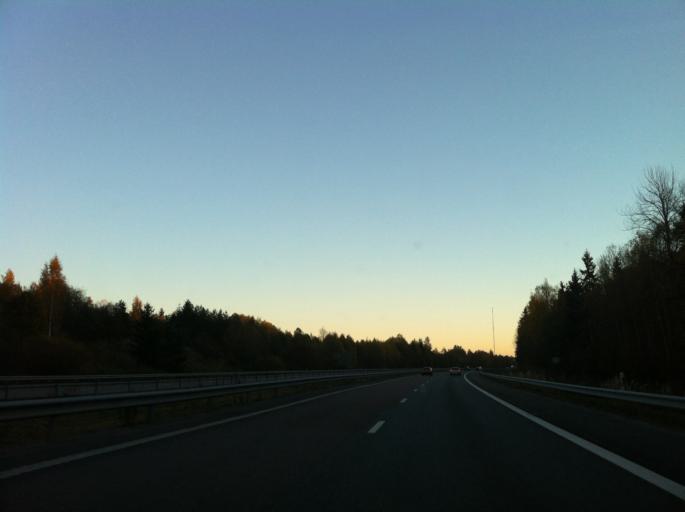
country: SE
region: Gaevleborg
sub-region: Gavle Kommun
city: Gavle
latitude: 60.6640
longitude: 17.1082
